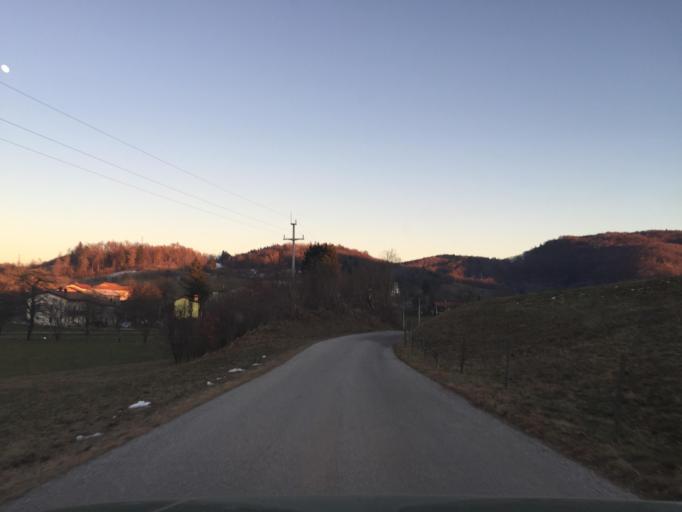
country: SI
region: Kanal
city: Kanal
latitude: 46.0784
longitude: 13.6589
